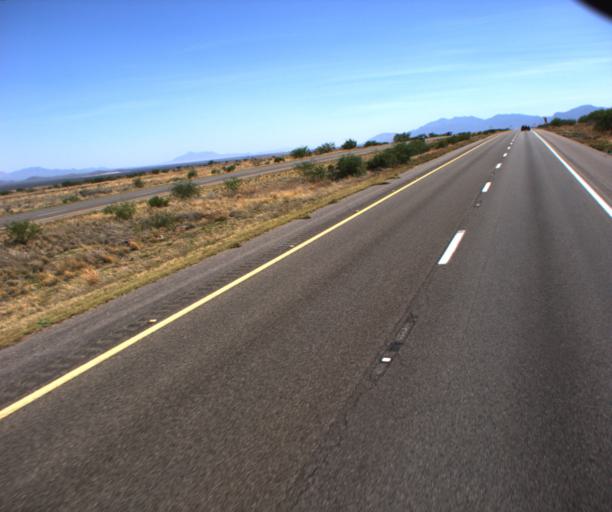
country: US
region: Arizona
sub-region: Cochise County
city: Huachuca City
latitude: 31.7875
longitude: -110.3503
